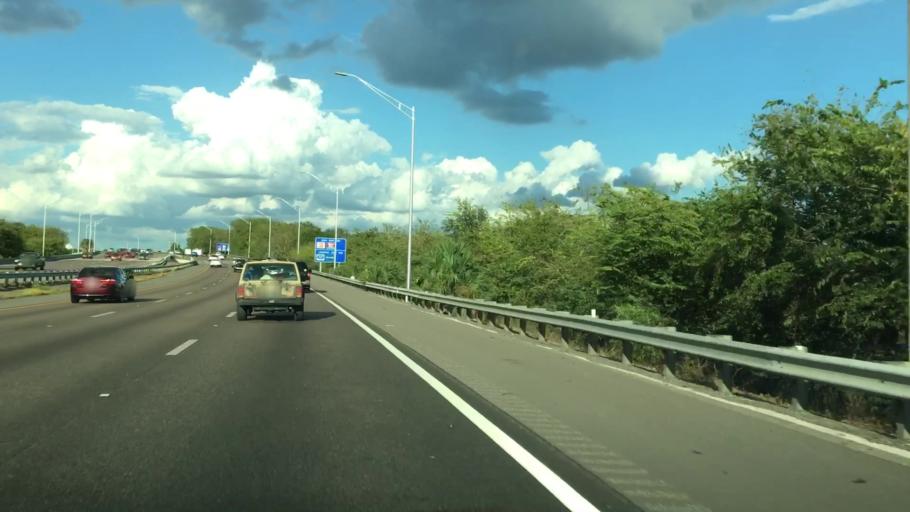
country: US
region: Florida
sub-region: Volusia County
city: DeBary
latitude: 28.8672
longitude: -81.2872
